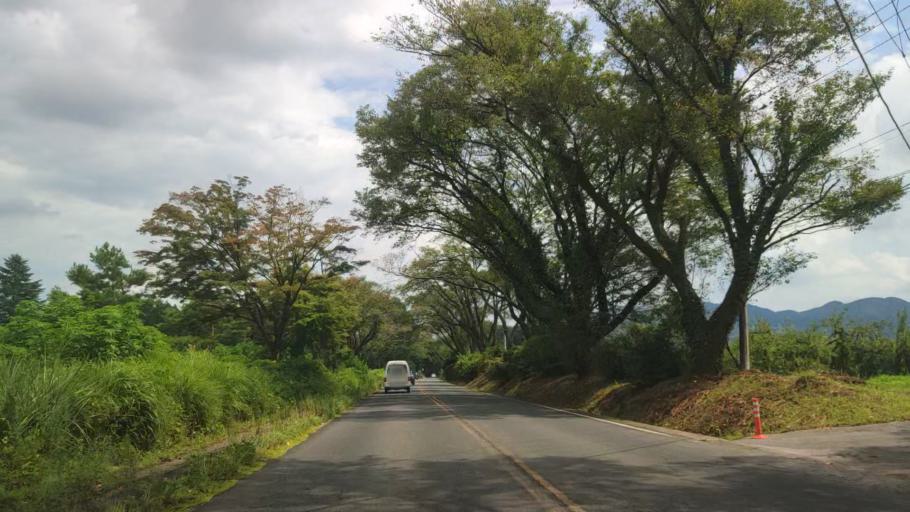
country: JP
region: Tochigi
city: Imaichi
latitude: 36.6788
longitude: 139.7966
